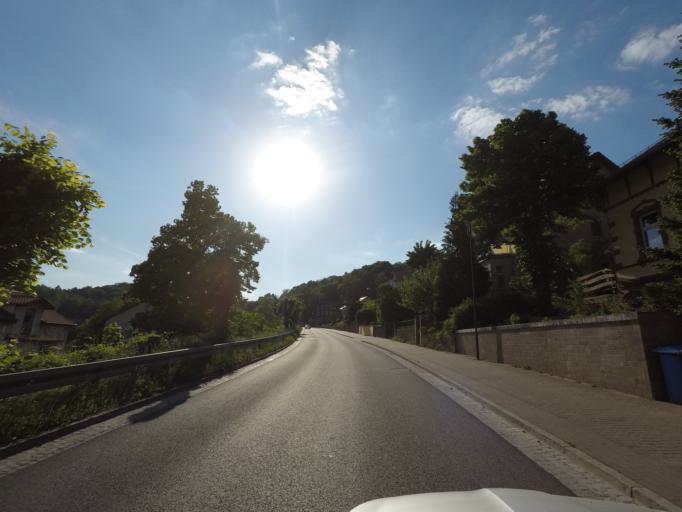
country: DE
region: Brandenburg
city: Falkenberg
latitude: 52.8047
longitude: 13.9545
